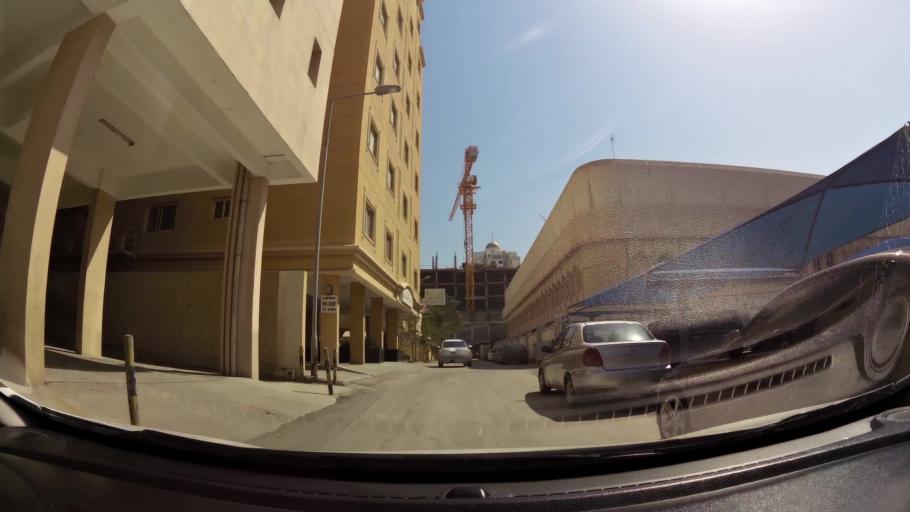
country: BH
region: Manama
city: Manama
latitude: 26.2136
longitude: 50.6019
